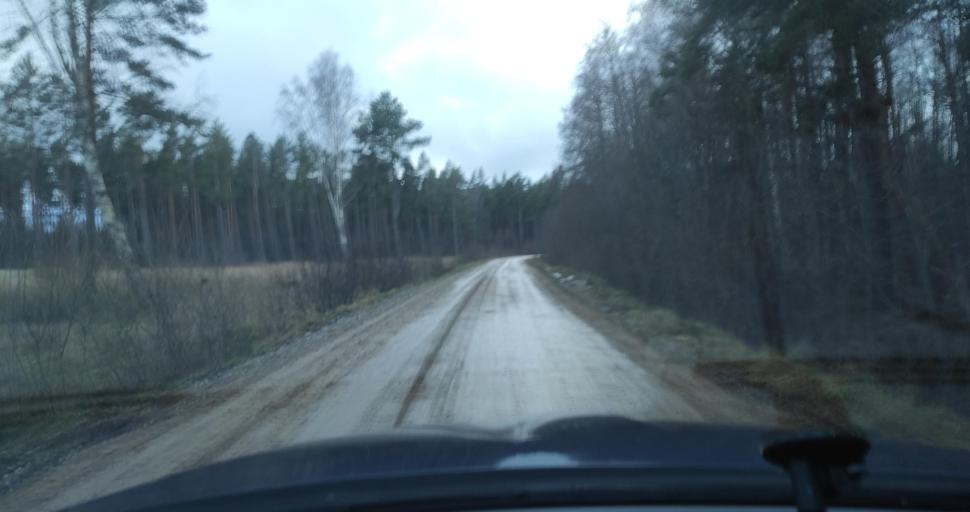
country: LV
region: Pavilostas
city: Pavilosta
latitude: 56.8408
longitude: 21.0842
